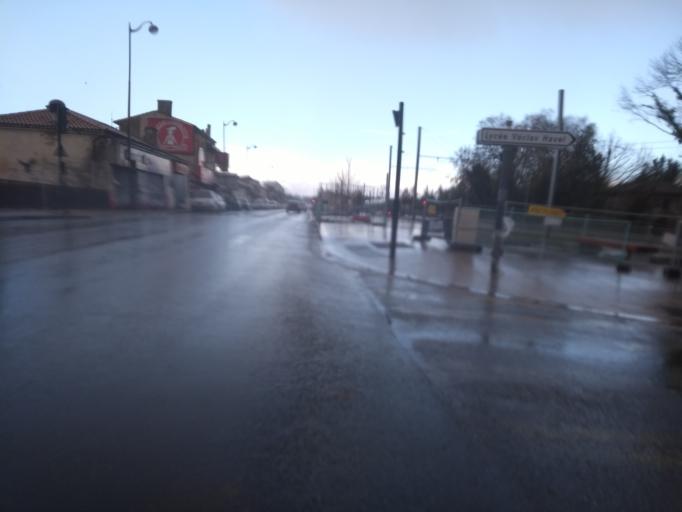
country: FR
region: Aquitaine
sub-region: Departement de la Gironde
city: Villenave-d'Ornon
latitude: 44.7857
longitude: -0.5664
